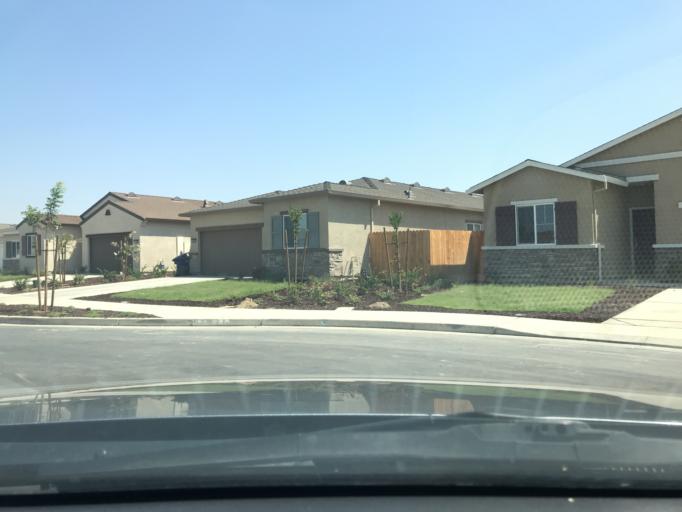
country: US
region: California
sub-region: Merced County
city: Merced
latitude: 37.3528
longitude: -120.4754
